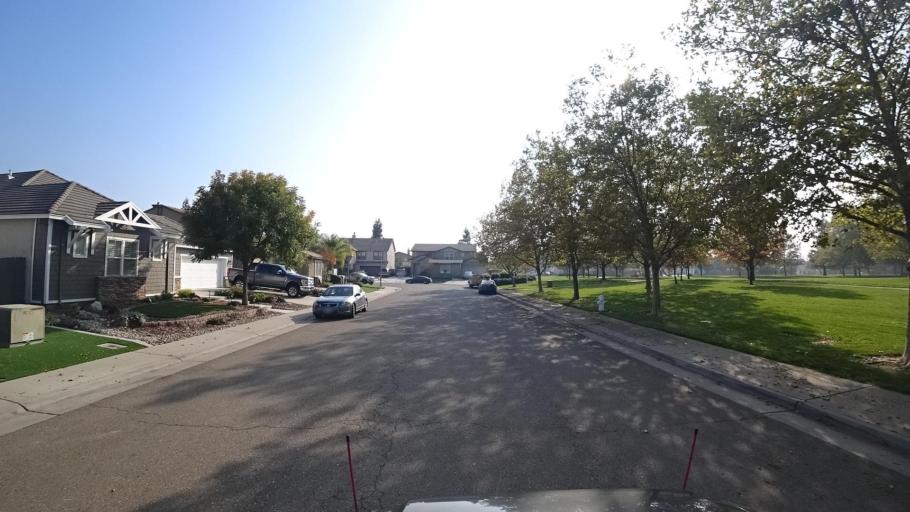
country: US
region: California
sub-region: Sacramento County
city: Elk Grove
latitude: 38.4159
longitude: -121.3398
